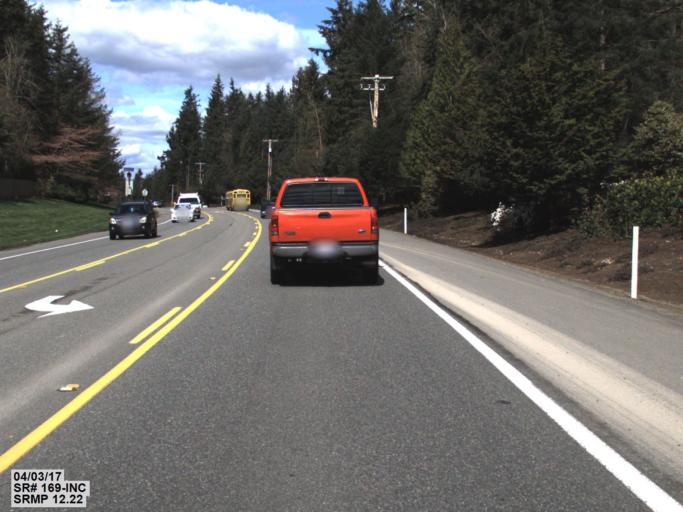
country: US
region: Washington
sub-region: King County
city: Maple Valley
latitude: 47.3726
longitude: -122.0234
